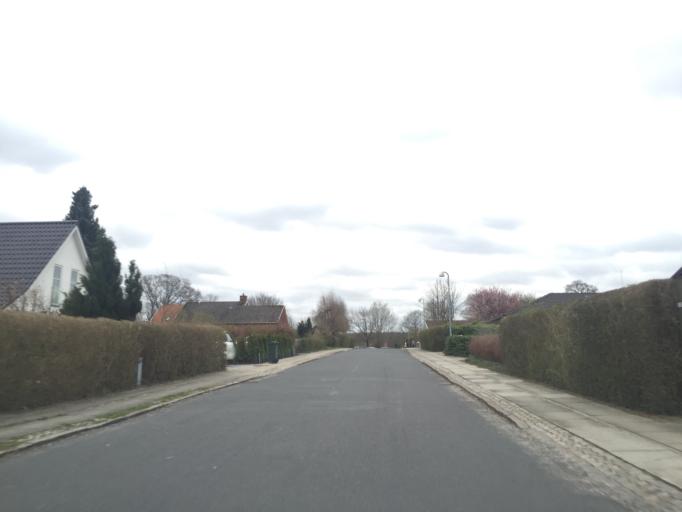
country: DK
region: Capital Region
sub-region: Rudersdal Kommune
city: Holte
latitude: 55.7894
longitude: 12.4525
